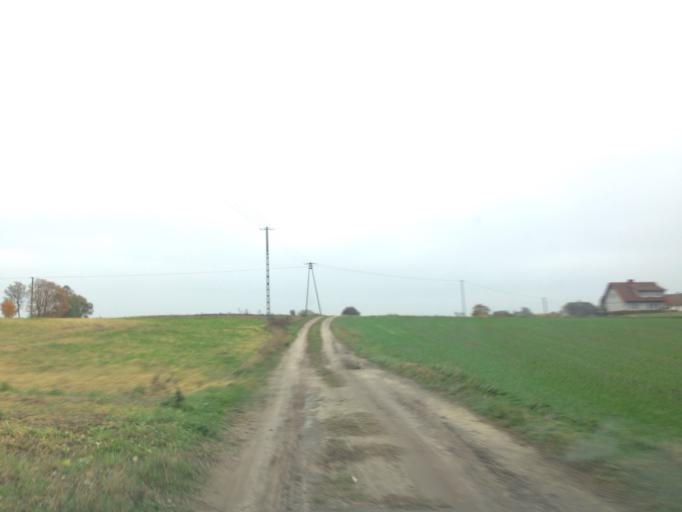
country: PL
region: Kujawsko-Pomorskie
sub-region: Powiat brodnicki
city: Gorzno
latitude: 53.2120
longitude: 19.6177
